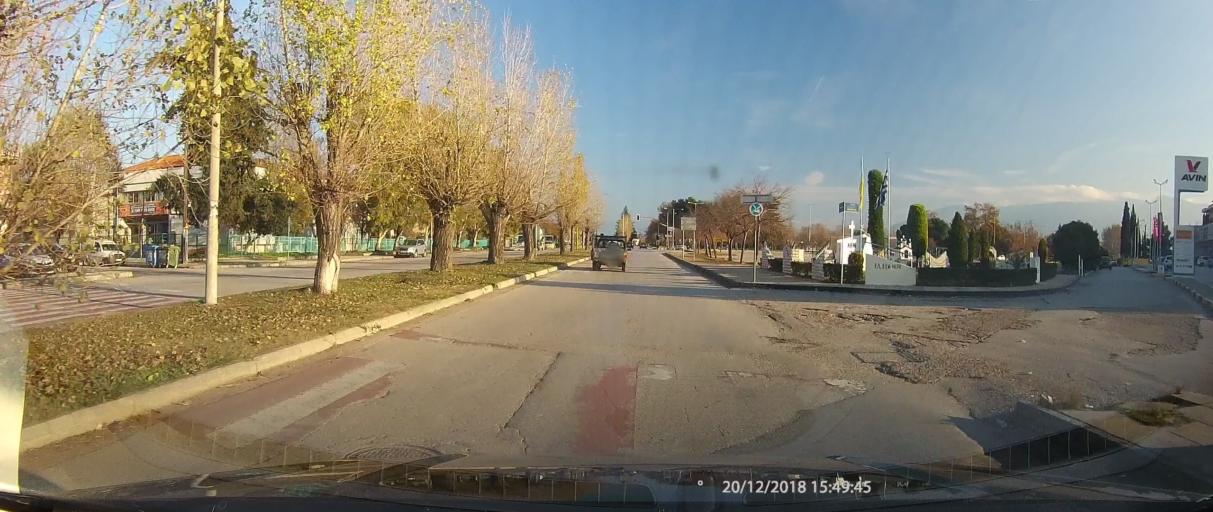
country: GR
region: Central Greece
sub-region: Nomos Fthiotidos
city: Lamia
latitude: 38.8940
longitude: 22.4453
